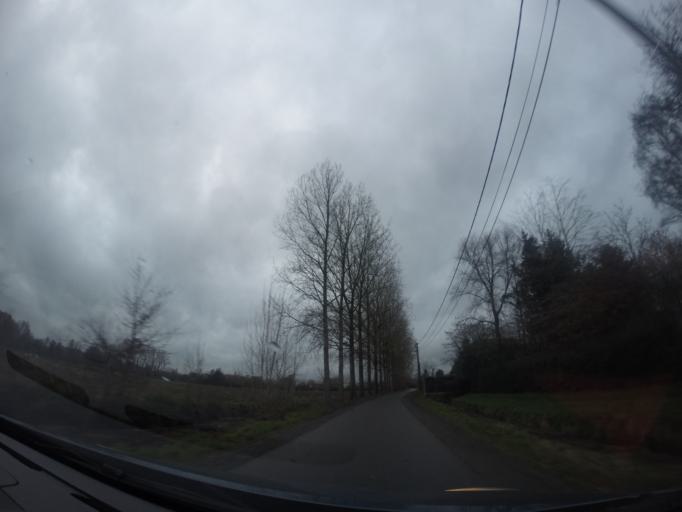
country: BE
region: Flanders
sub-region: Provincie Oost-Vlaanderen
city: Nevele
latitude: 51.0708
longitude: 3.5163
